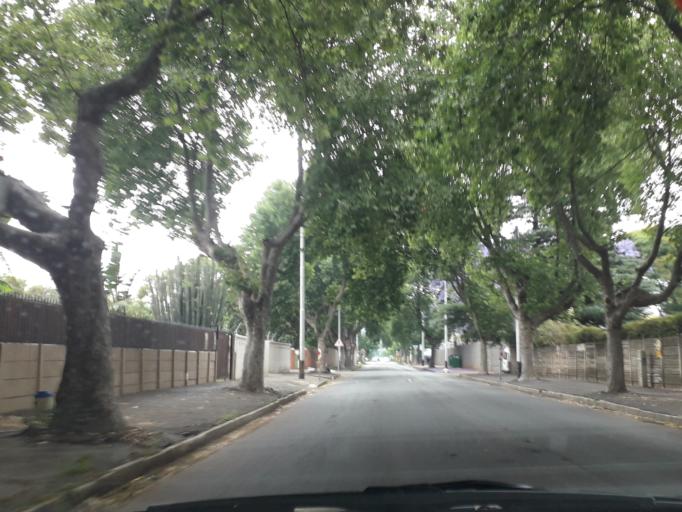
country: ZA
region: Gauteng
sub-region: City of Johannesburg Metropolitan Municipality
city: Johannesburg
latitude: -26.1550
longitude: 28.0900
